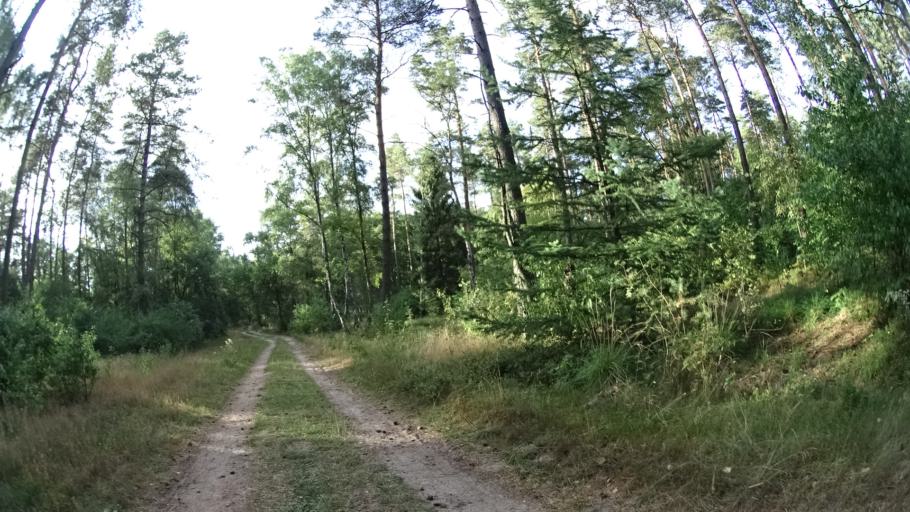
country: DE
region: Lower Saxony
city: Handeloh
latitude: 53.2211
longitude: 9.8781
